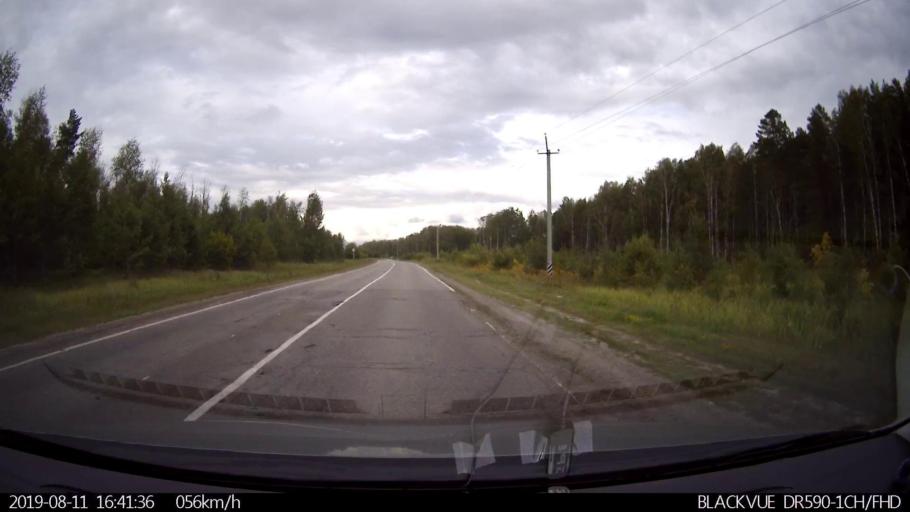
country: RU
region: Ulyanovsk
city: Mayna
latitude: 54.1545
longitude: 47.6541
